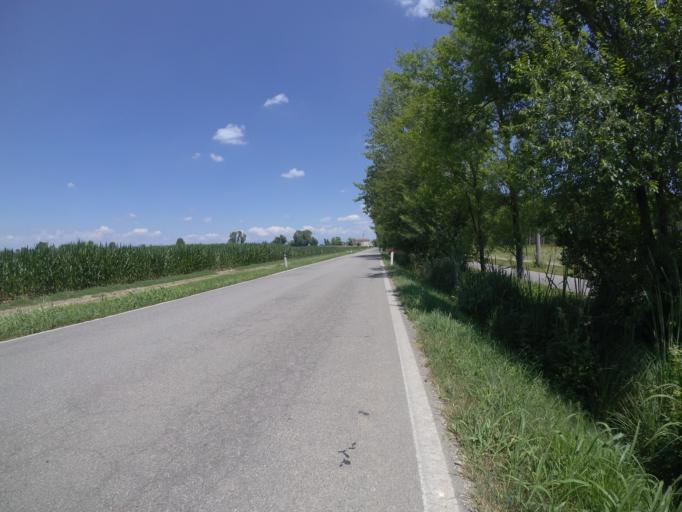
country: IT
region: Friuli Venezia Giulia
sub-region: Provincia di Udine
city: Varmo
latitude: 45.9267
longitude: 13.0020
